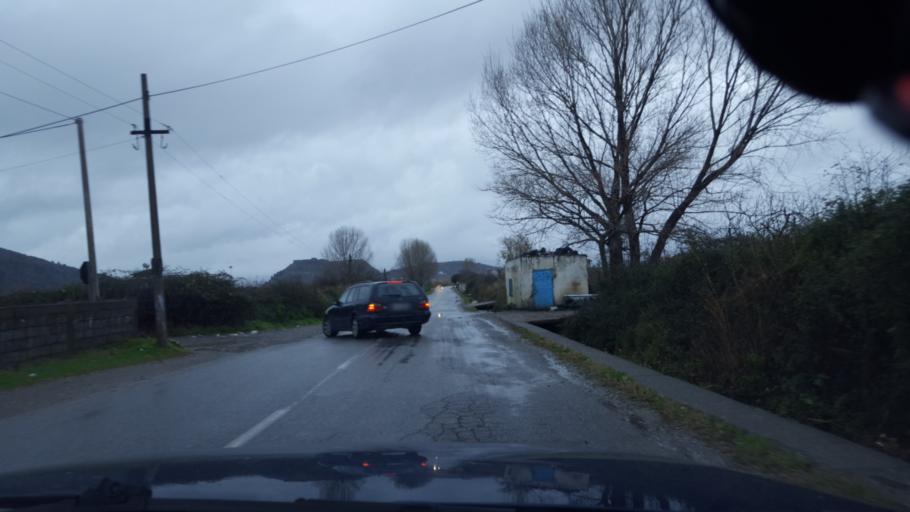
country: AL
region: Shkoder
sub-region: Rrethi i Shkodres
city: Berdica e Madhe
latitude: 42.0234
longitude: 19.4866
